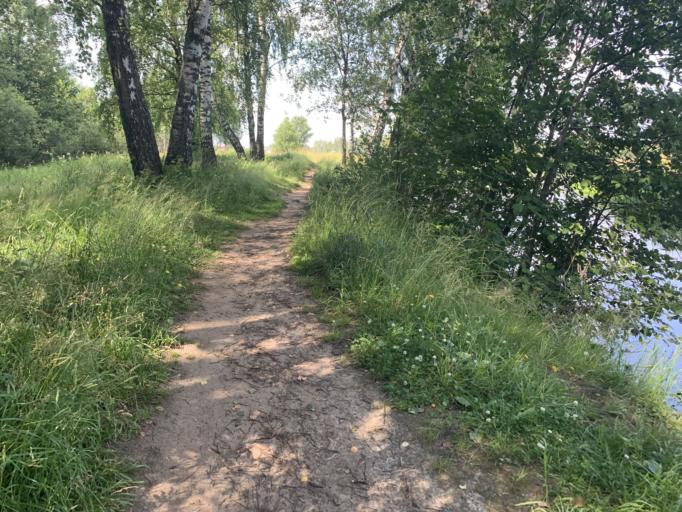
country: RU
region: Moskovskaya
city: Cherkizovo
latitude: 55.9739
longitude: 37.8007
